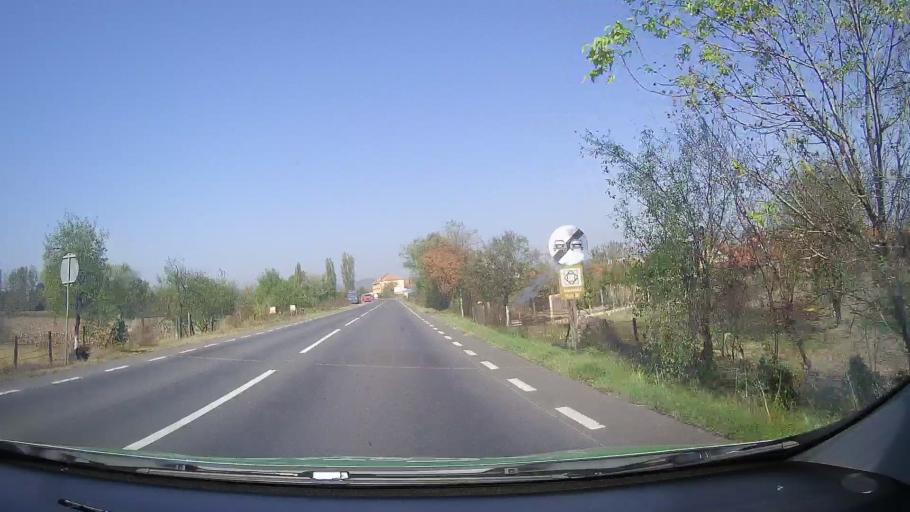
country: RO
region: Hunedoara
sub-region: Comuna Ilia
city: Ilia
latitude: 45.9288
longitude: 22.6590
